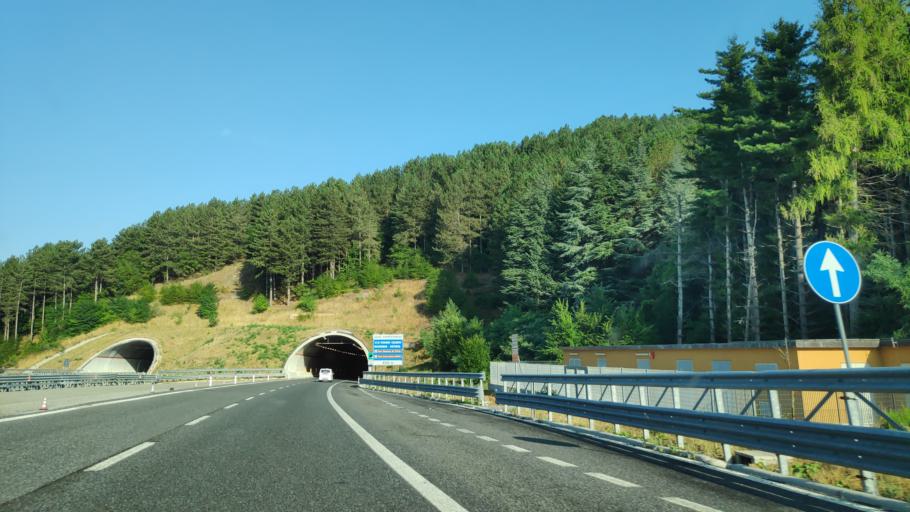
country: IT
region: Calabria
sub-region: Provincia di Cosenza
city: Morano Calabro
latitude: 39.8644
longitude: 16.0844
